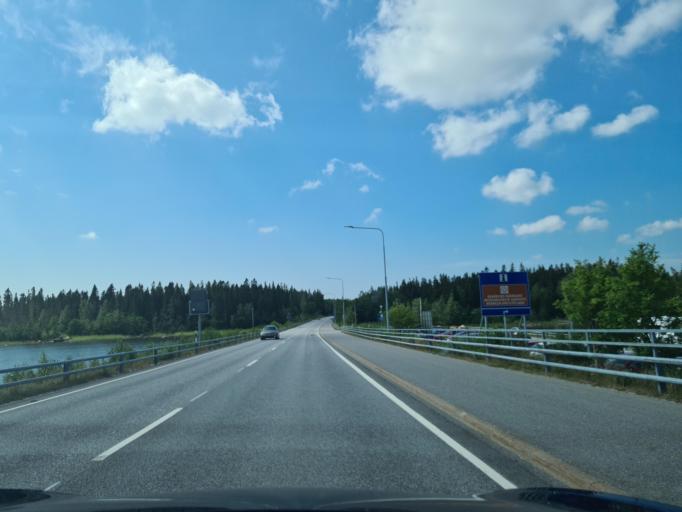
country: FI
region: Ostrobothnia
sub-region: Vaasa
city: Replot
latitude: 63.2067
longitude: 21.4603
